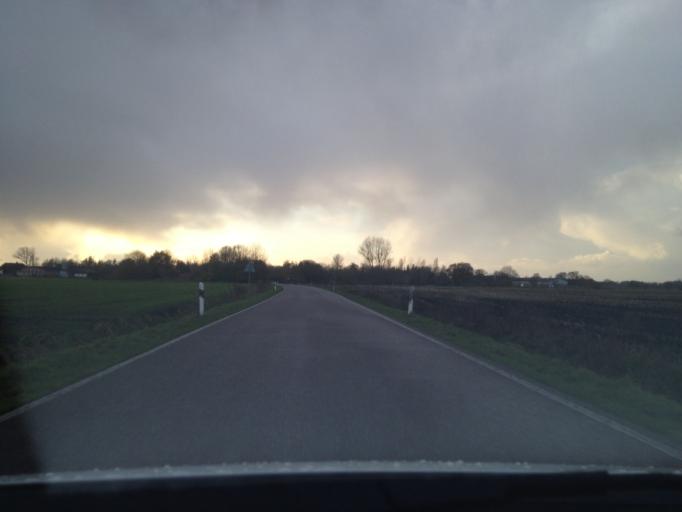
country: DE
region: Schleswig-Holstein
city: Braderup
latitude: 54.8356
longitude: 8.9032
